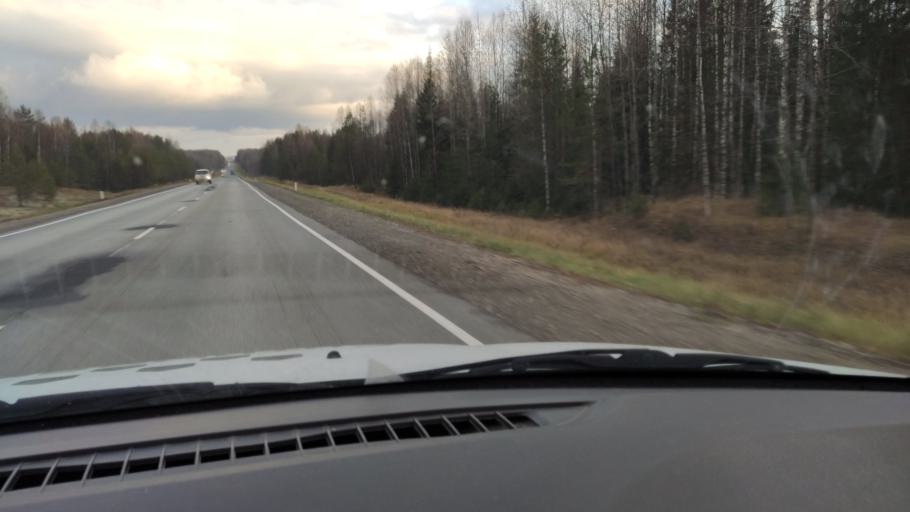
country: RU
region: Kirov
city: Chernaya Kholunitsa
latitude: 58.8090
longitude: 51.8400
